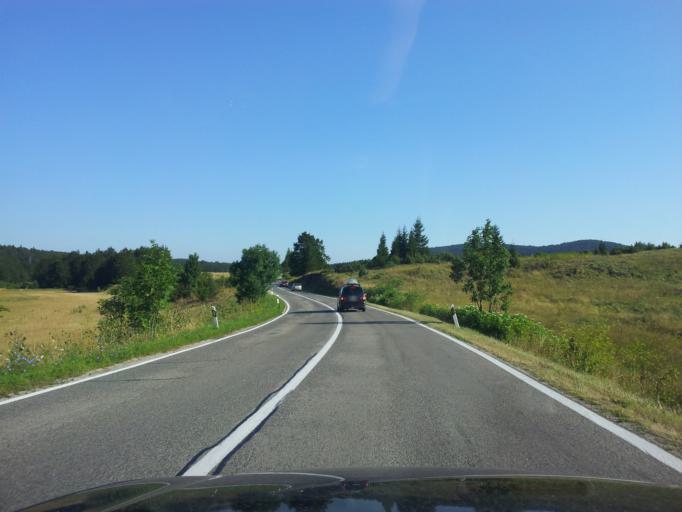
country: HR
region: Licko-Senjska
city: Jezerce
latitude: 44.8074
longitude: 15.6831
